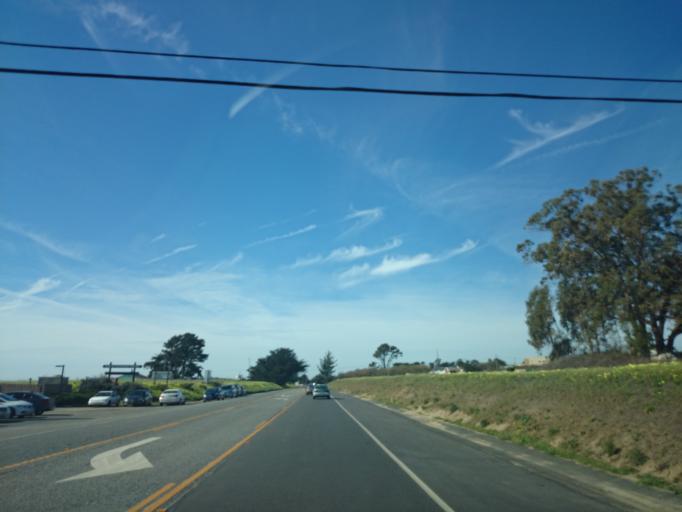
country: US
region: California
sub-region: San Mateo County
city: El Granada
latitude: 37.5029
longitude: -122.4753
